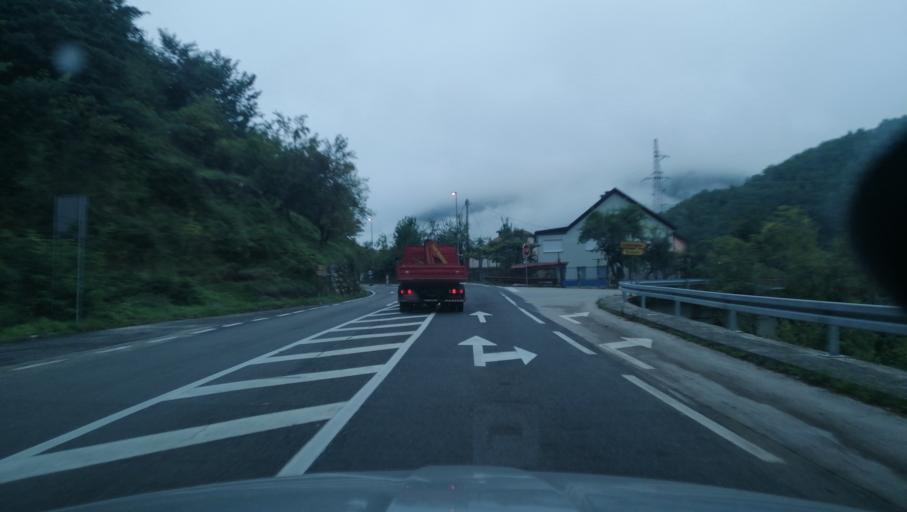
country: BA
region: Federation of Bosnia and Herzegovina
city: Jablanica
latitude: 43.7230
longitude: 17.7050
